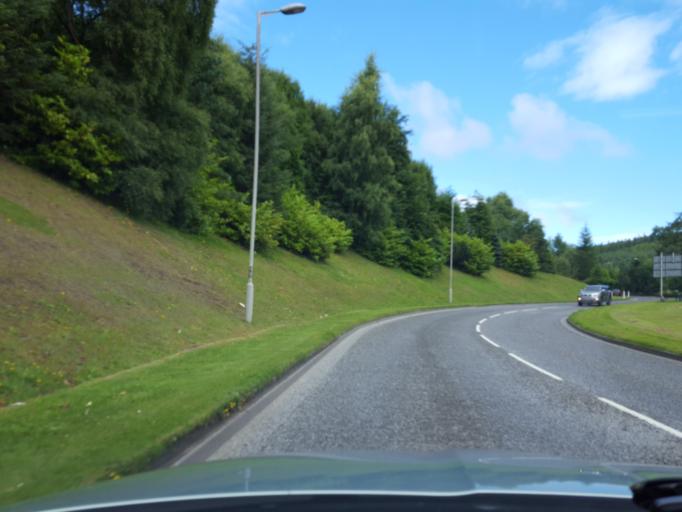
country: GB
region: Scotland
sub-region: Moray
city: Rothes
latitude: 57.5314
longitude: -3.2089
